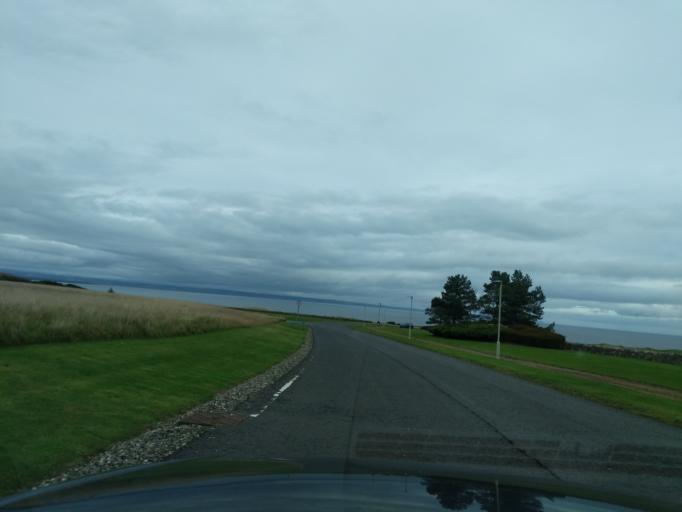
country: GB
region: Scotland
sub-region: Fife
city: Saint Andrews
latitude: 56.3197
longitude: -2.7377
